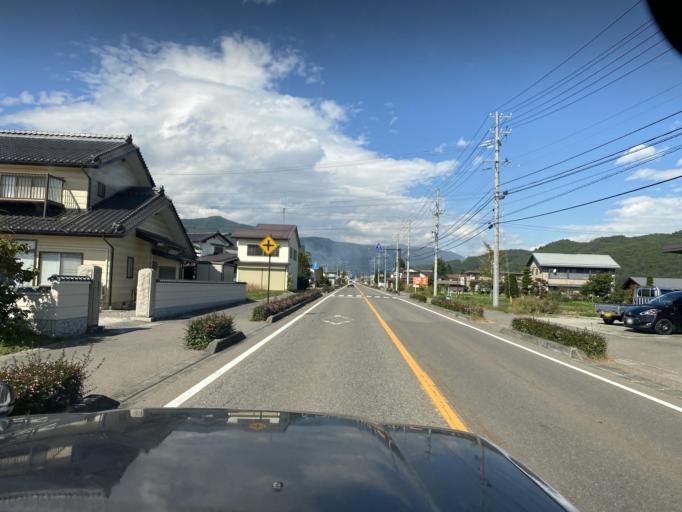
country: JP
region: Nagano
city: Omachi
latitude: 36.5243
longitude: 137.8512
